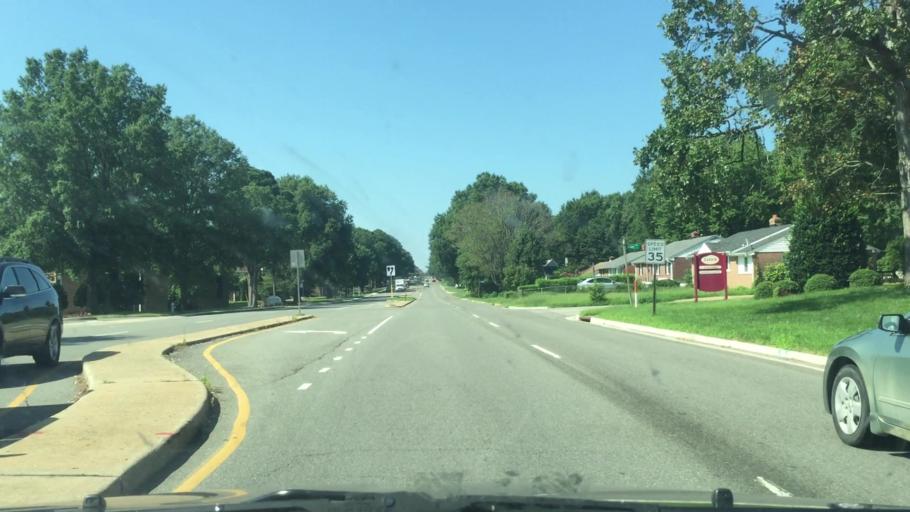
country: US
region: Virginia
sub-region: Henrico County
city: Dumbarton
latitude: 37.5897
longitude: -77.5044
